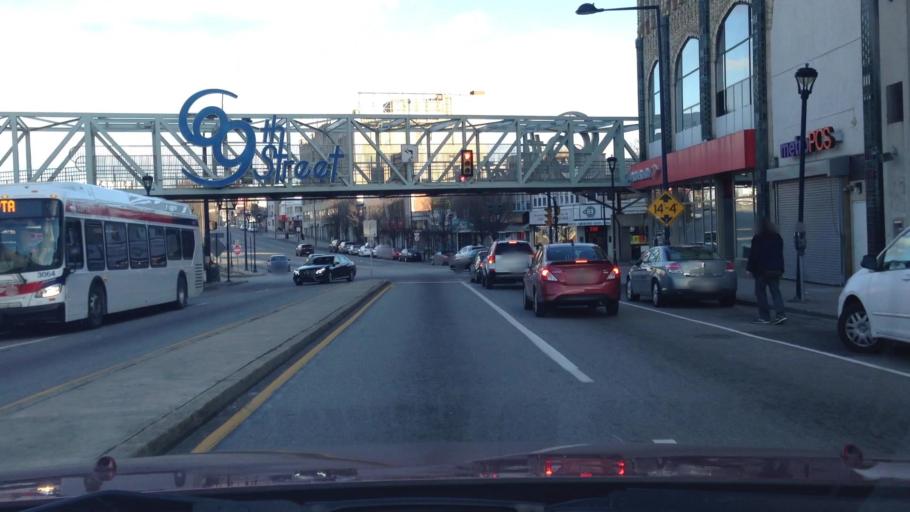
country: US
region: Pennsylvania
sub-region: Delaware County
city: Millbourne
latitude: 39.9618
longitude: -75.2598
